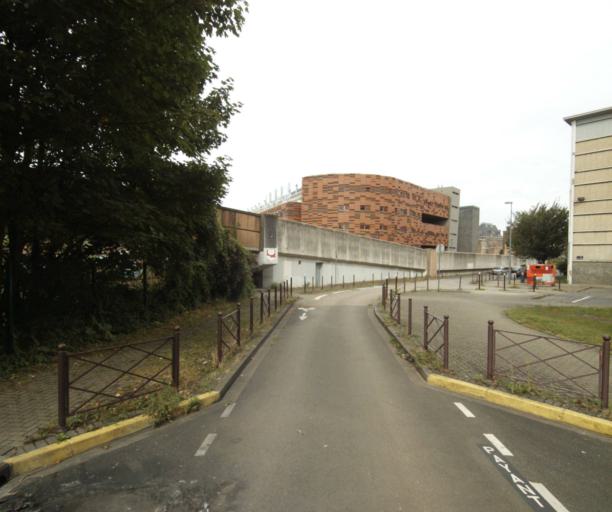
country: FR
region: Nord-Pas-de-Calais
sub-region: Departement du Nord
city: La Madeleine
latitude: 50.6272
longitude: 3.0771
